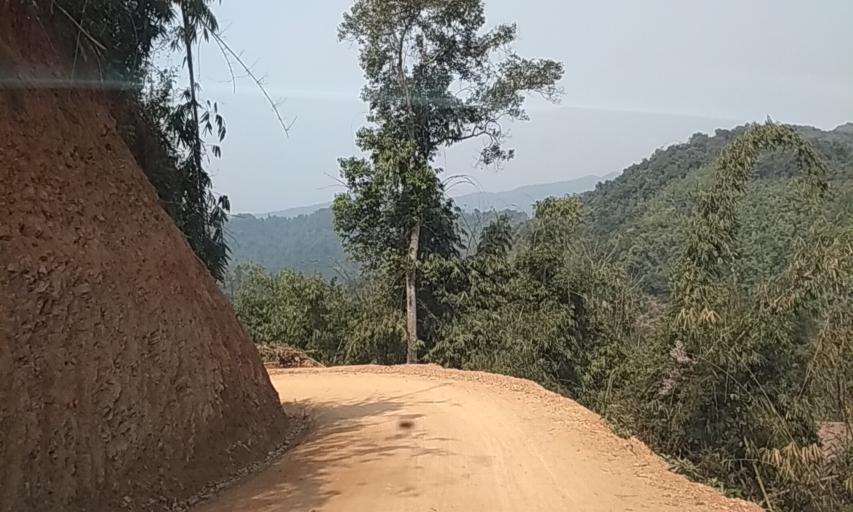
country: LA
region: Phongsali
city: Phongsali
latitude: 21.4725
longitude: 102.4333
